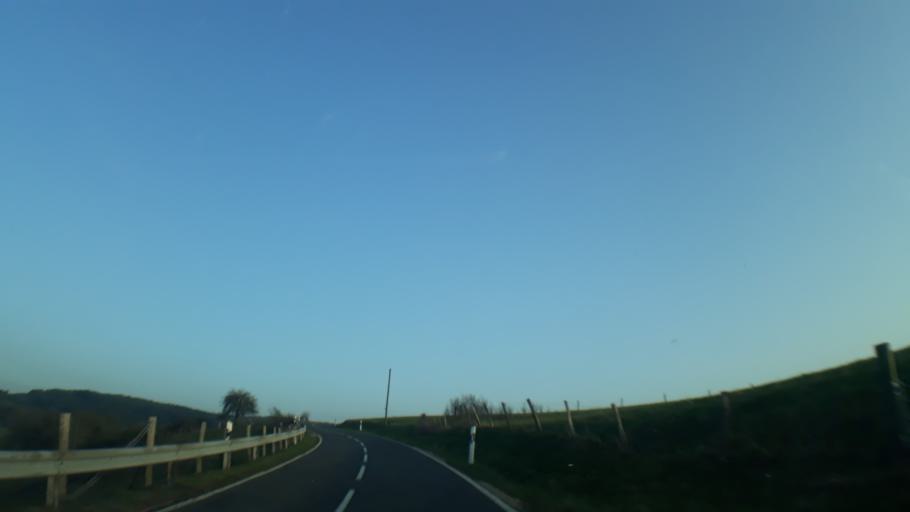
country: DE
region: Rheinland-Pfalz
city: Hummel
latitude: 50.5081
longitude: 6.7792
